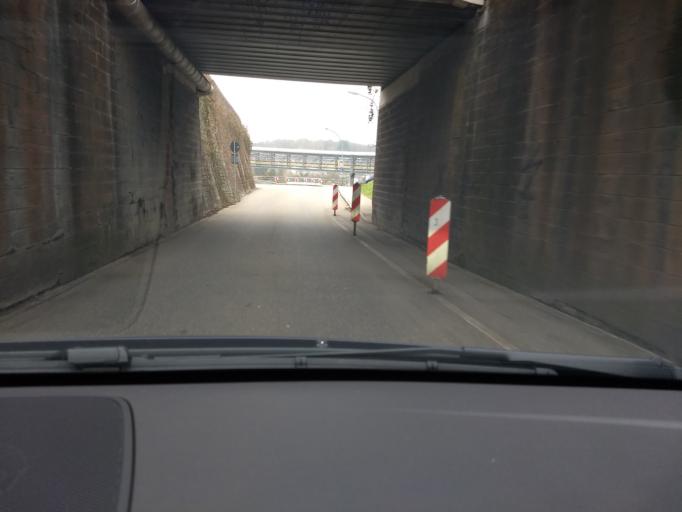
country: CH
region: Aargau
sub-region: Bezirk Rheinfelden
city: Rheinfelden
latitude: 47.5658
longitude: 7.8001
